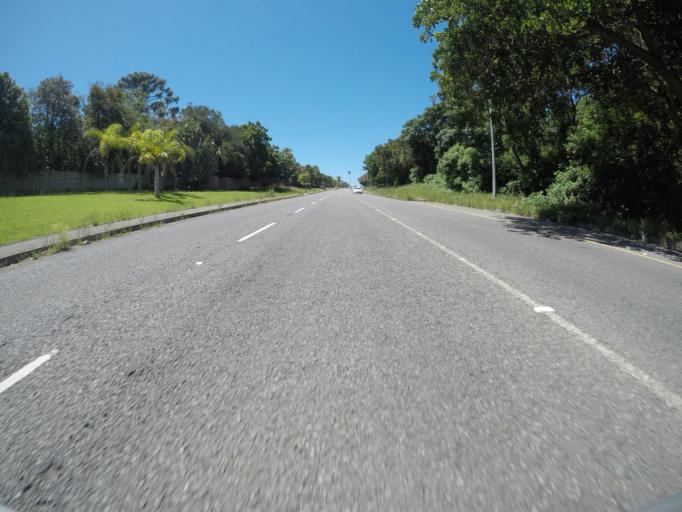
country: ZA
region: Eastern Cape
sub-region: Buffalo City Metropolitan Municipality
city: East London
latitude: -32.9666
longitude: 27.9314
